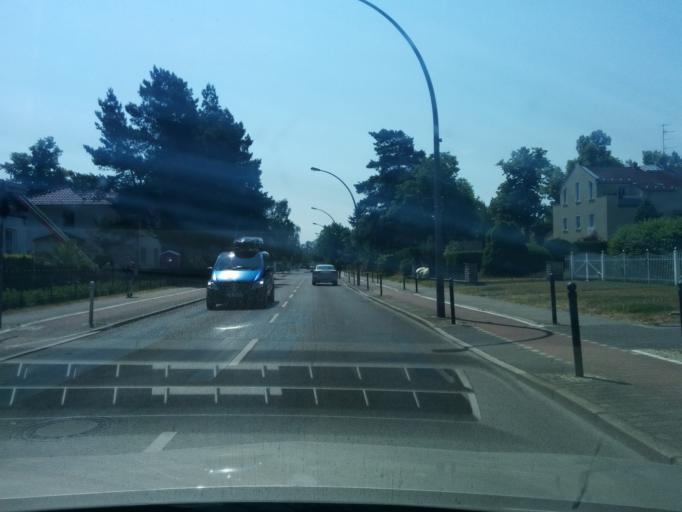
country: DE
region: Berlin
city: Bohnsdorf
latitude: 52.4034
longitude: 13.5734
